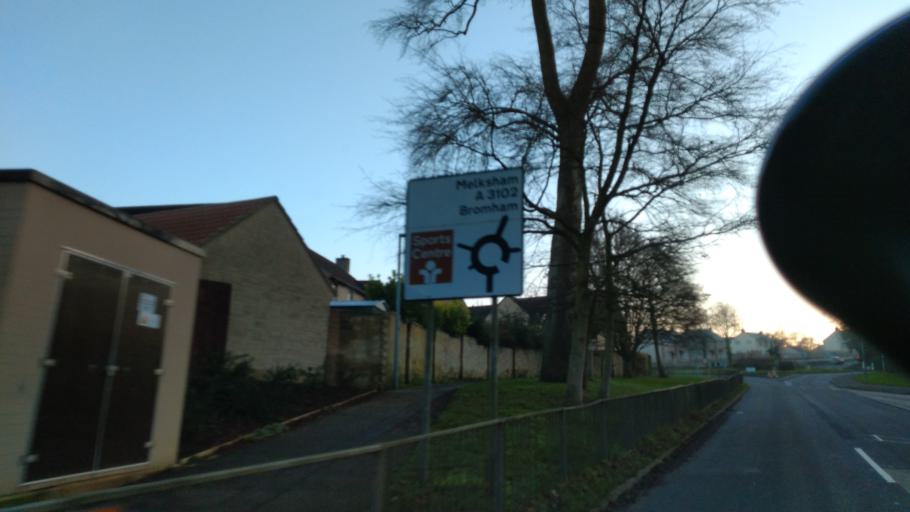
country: GB
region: England
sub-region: Wiltshire
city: Calne
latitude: 51.4328
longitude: -2.0045
